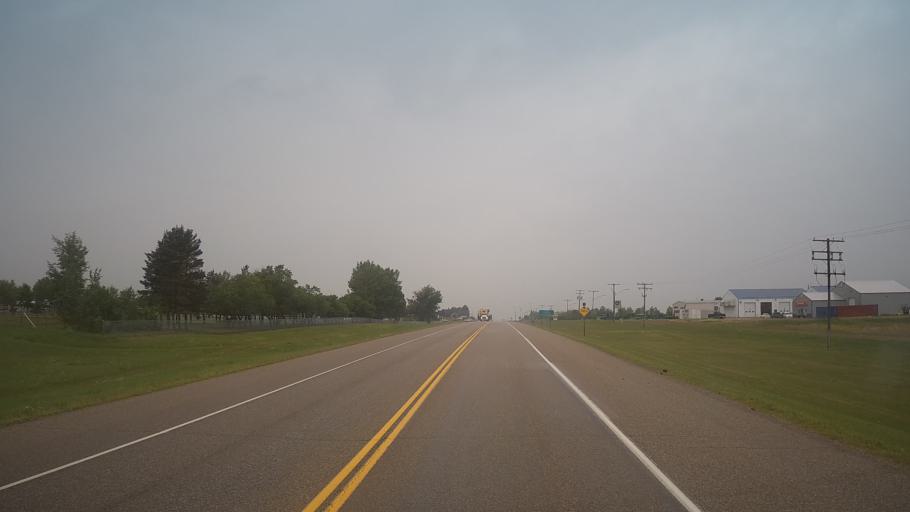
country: CA
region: Saskatchewan
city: Biggar
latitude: 52.0610
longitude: -107.9725
